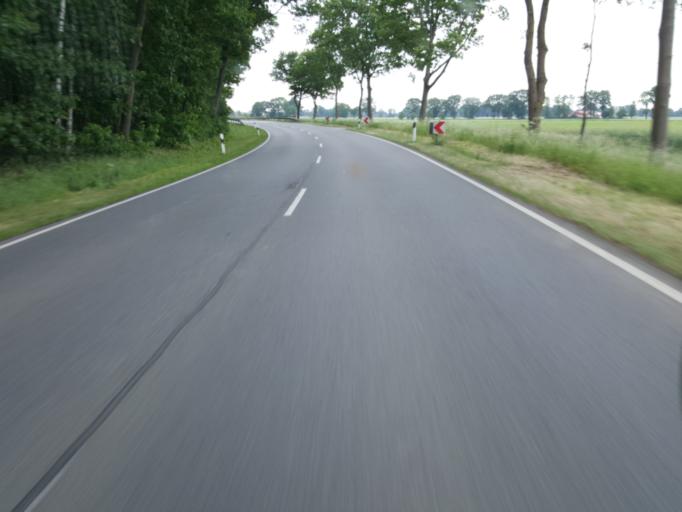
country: DE
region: Lower Saxony
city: Leese
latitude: 52.4832
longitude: 9.1348
